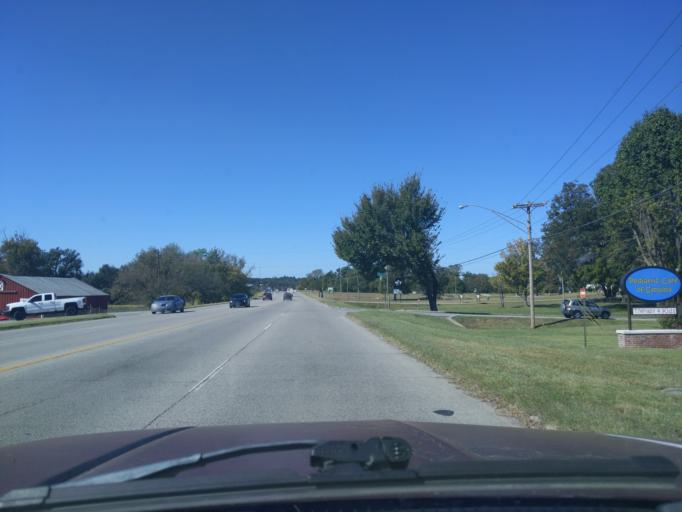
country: US
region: Oklahoma
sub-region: Creek County
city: Sapulpa
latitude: 35.9885
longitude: -96.1234
